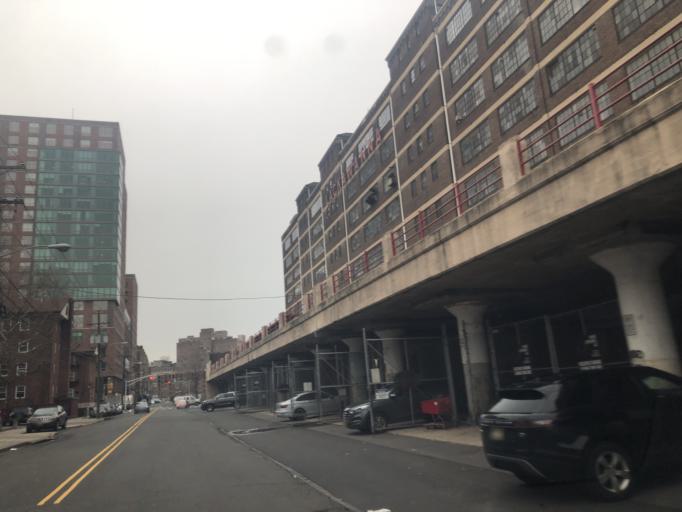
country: US
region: New Jersey
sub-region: Hudson County
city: Hoboken
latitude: 40.7333
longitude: -74.0428
